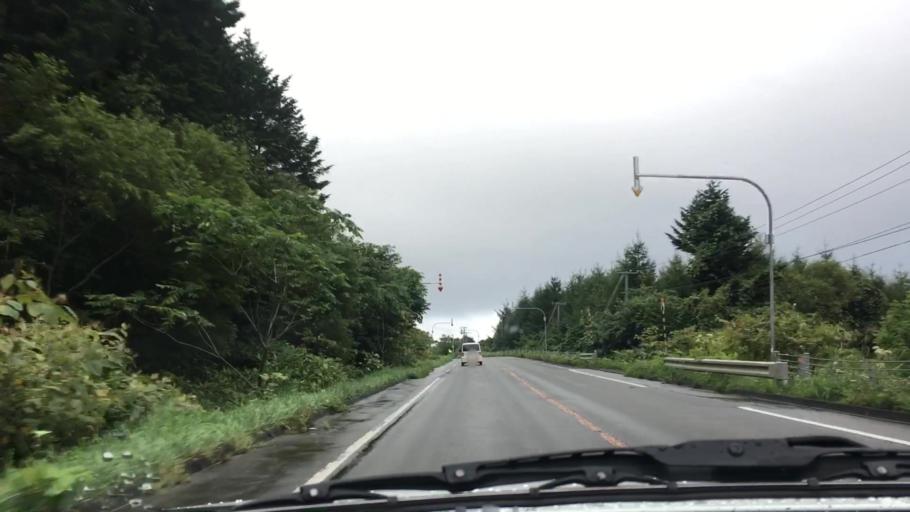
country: JP
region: Hokkaido
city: Niseko Town
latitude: 42.6023
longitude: 140.7246
